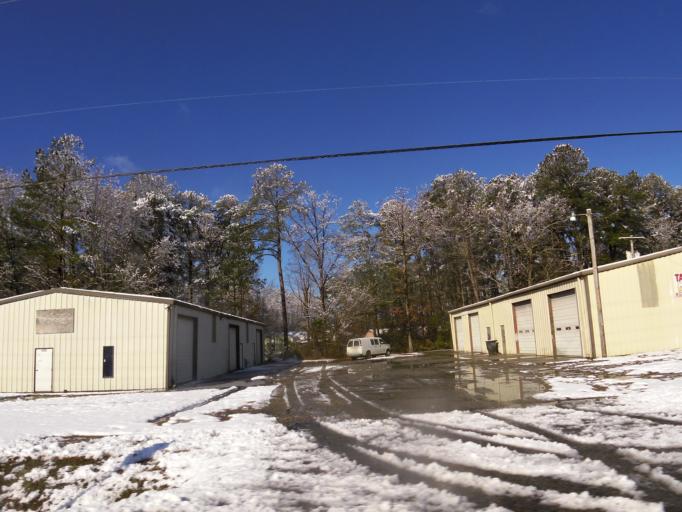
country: US
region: North Carolina
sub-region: Nash County
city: Sharpsburg
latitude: 35.8599
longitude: -77.8340
